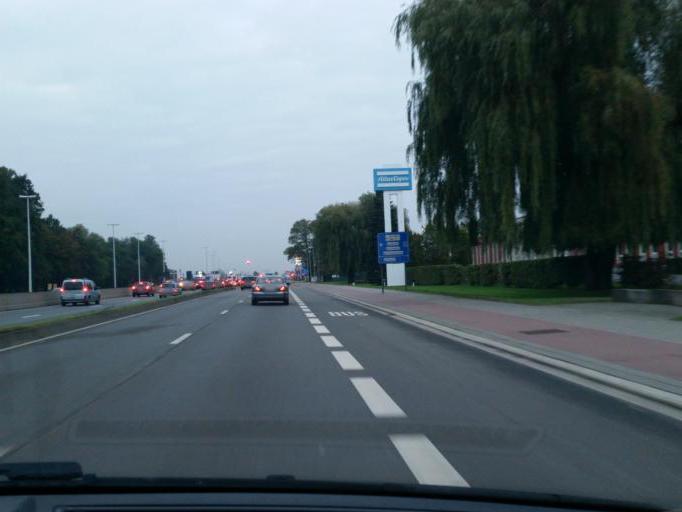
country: BE
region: Flanders
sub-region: Provincie Antwerpen
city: Aartselaar
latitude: 51.1498
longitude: 4.3817
